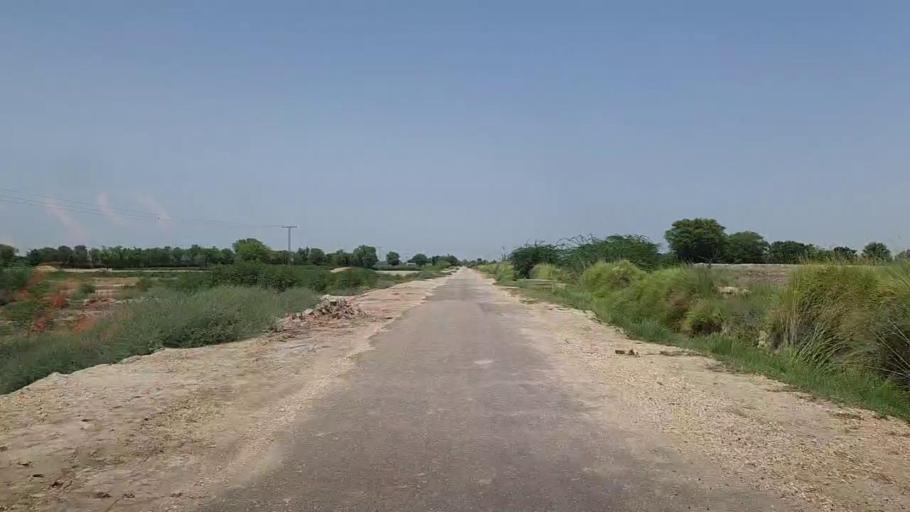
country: PK
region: Sindh
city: Pad Idan
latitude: 26.7489
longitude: 68.3154
